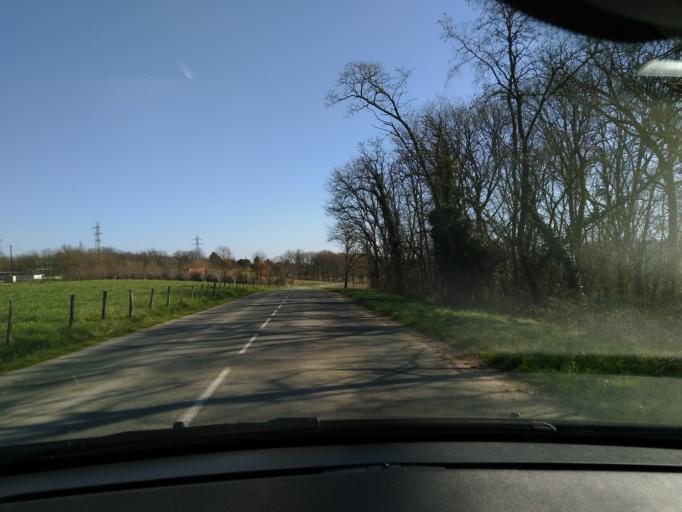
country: FR
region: Aquitaine
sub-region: Departement du Lot-et-Garonne
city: Cancon
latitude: 44.5358
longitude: 0.6434
